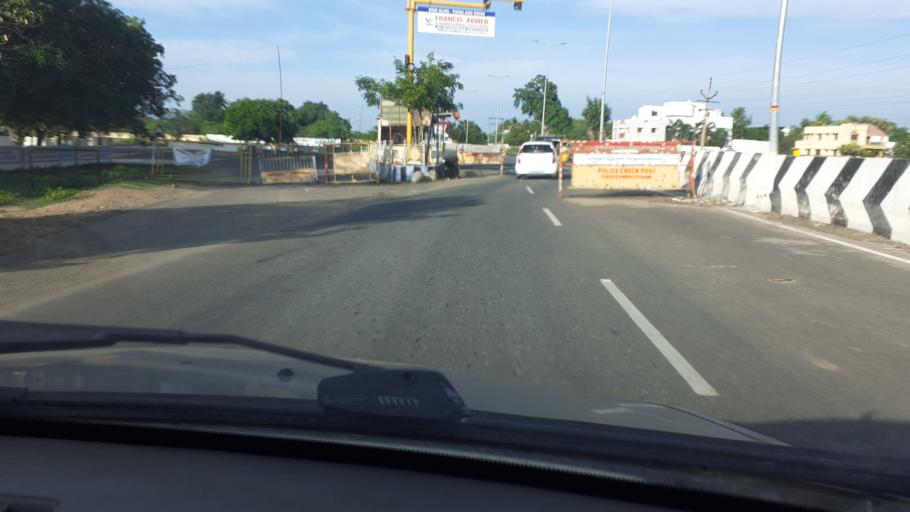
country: IN
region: Tamil Nadu
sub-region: Tirunelveli Kattabo
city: Tirunelveli
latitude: 8.6779
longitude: 77.7223
